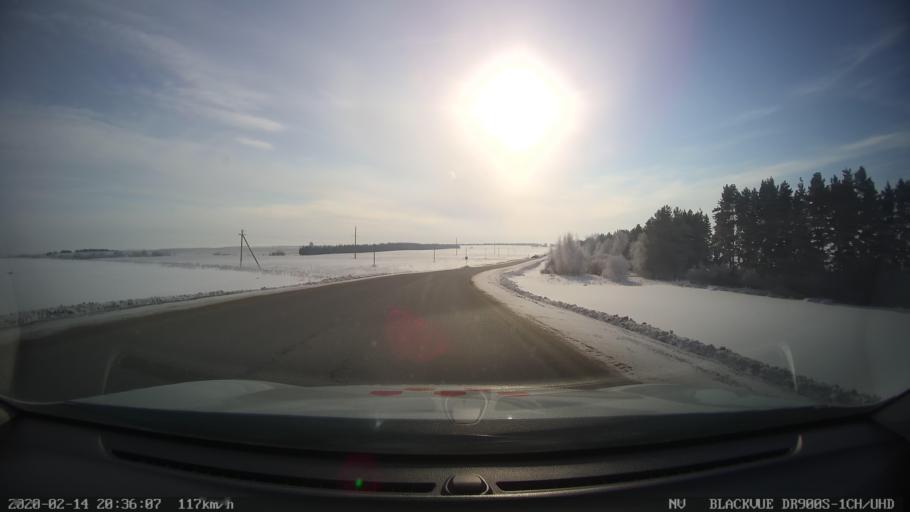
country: RU
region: Tatarstan
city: Kuybyshevskiy Zaton
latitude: 55.3738
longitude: 48.9956
